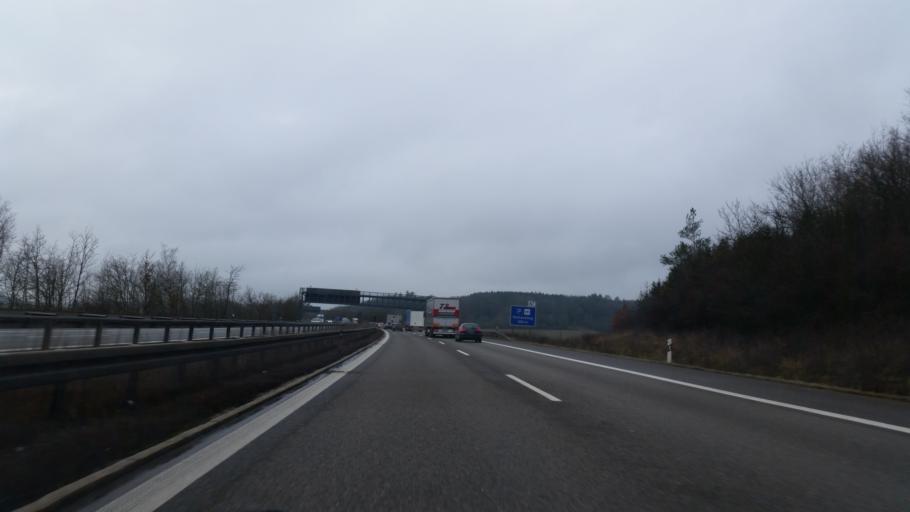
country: DE
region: Bavaria
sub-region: Regierungsbezirk Mittelfranken
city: Schnelldorf
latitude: 49.2057
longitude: 10.2134
